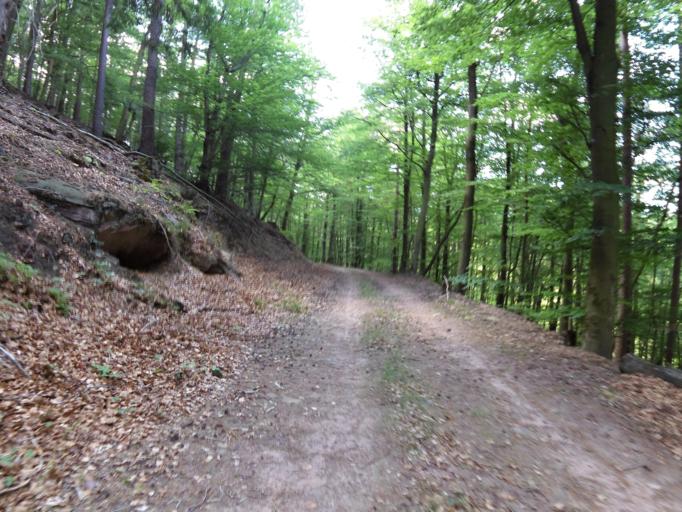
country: DE
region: Rheinland-Pfalz
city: Waldleiningen
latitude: 49.3782
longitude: 7.8586
